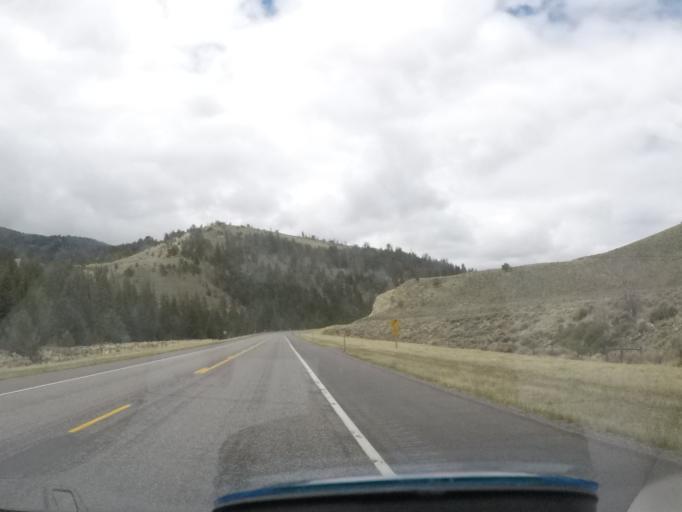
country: US
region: Wyoming
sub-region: Sublette County
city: Pinedale
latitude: 43.5790
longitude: -109.7552
